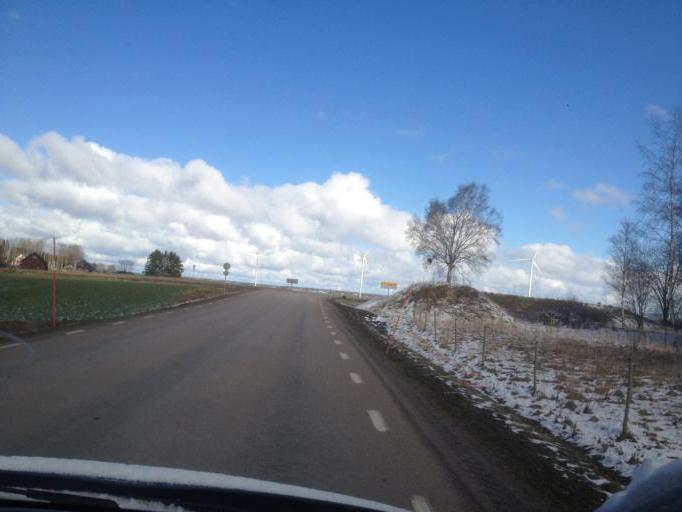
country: SE
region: OEstergoetland
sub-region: Mjolby Kommun
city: Mantorp
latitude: 58.4206
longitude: 15.3335
